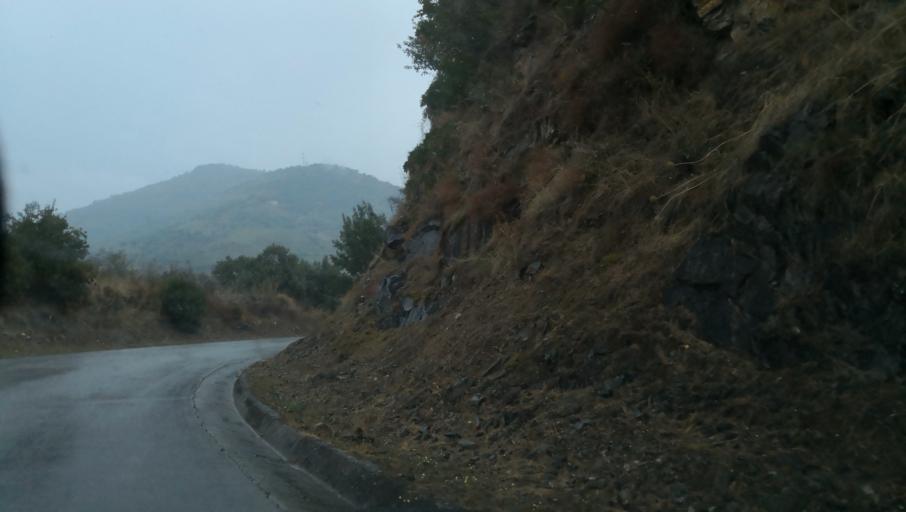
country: PT
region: Vila Real
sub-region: Peso da Regua
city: Peso da Regua
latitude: 41.1730
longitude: -7.7493
